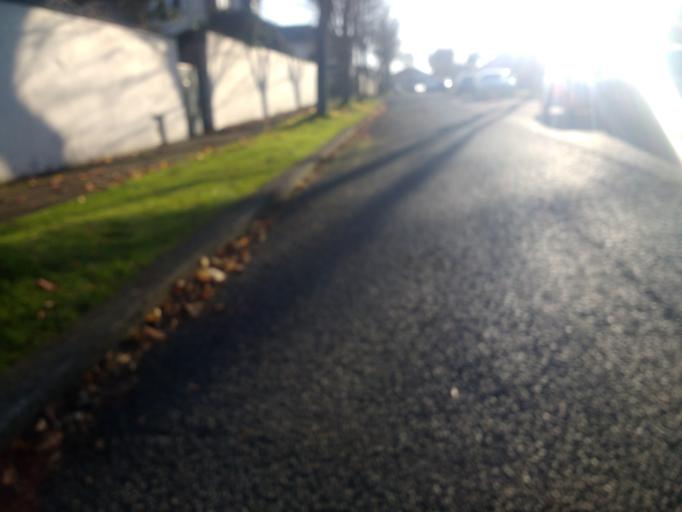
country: IE
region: Leinster
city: Kinsealy-Drinan
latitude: 53.4564
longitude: -6.1840
